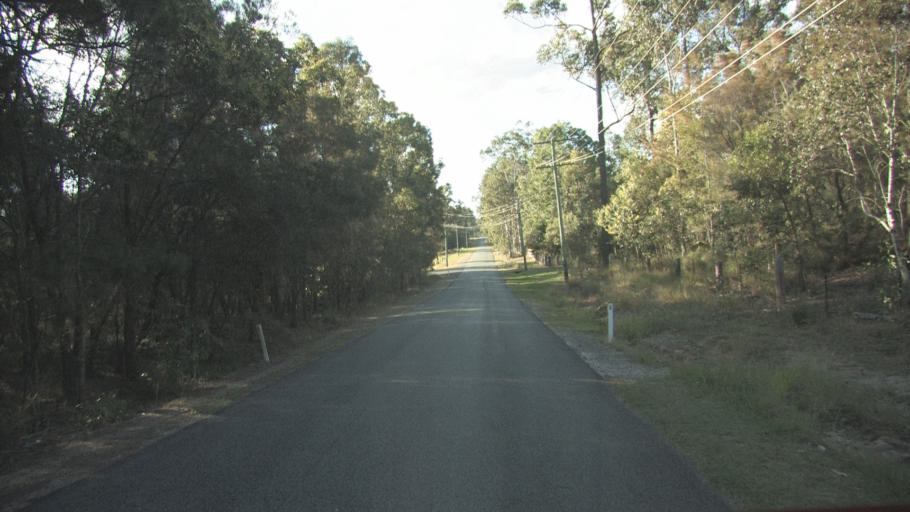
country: AU
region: Queensland
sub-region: Ipswich
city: Springfield Lakes
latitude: -27.7011
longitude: 152.9483
